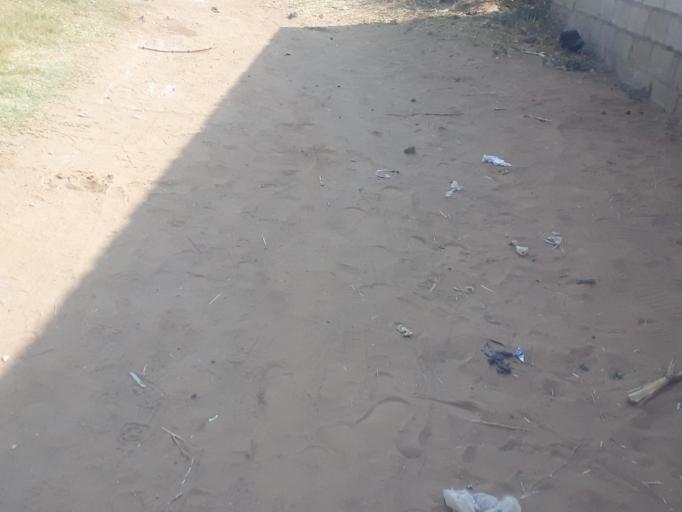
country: ZM
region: Lusaka
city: Lusaka
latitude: -15.3584
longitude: 28.3004
